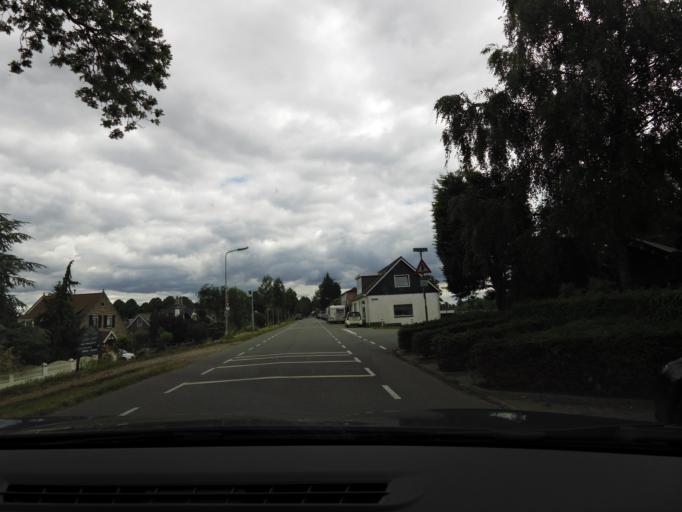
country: NL
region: South Holland
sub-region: Gemeente Oud-Beijerland
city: Oud-Beijerland
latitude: 51.7686
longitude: 4.4341
